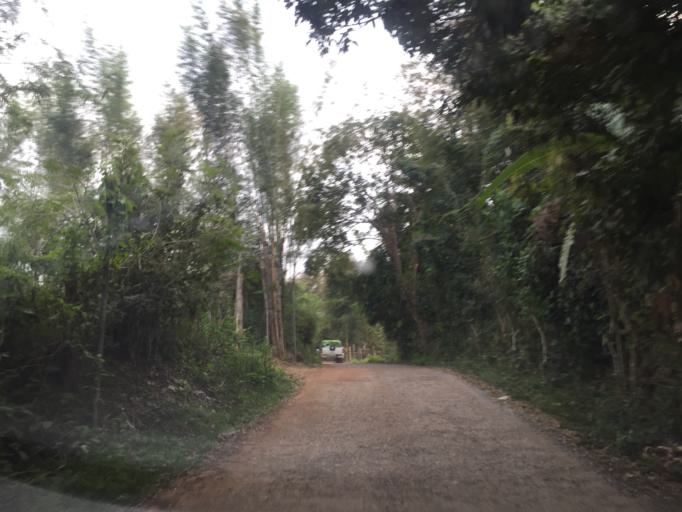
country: TH
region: Chiang Mai
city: Samoeng
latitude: 18.9945
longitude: 98.7276
